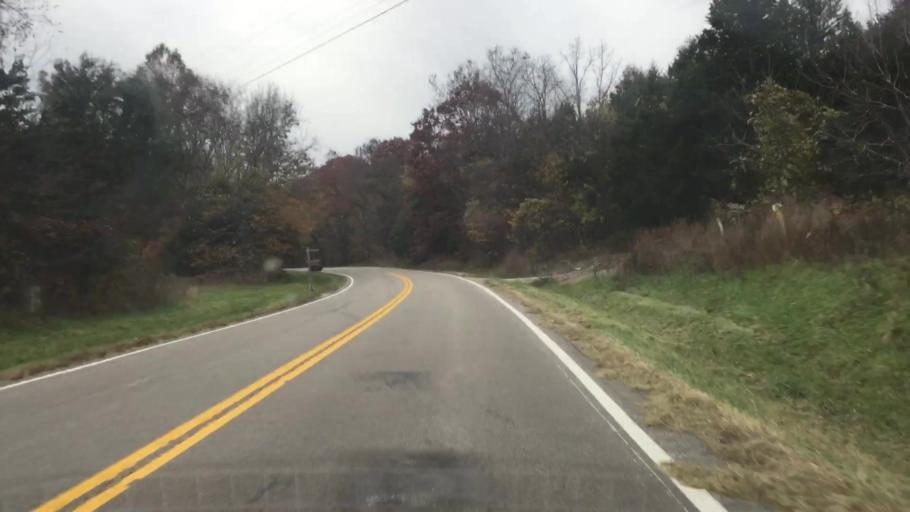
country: US
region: Missouri
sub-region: Gasconade County
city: Hermann
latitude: 38.7223
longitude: -91.6932
